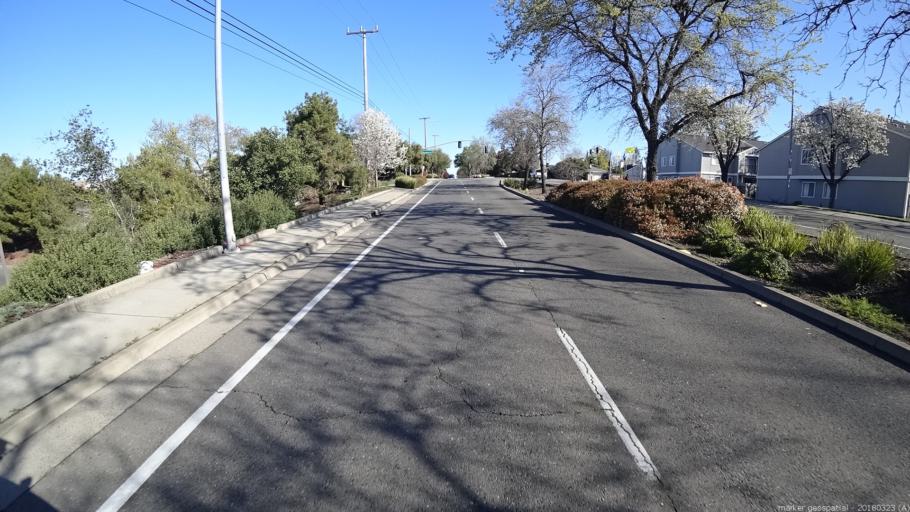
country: US
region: California
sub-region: Sacramento County
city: North Highlands
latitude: 38.7161
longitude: -121.3646
